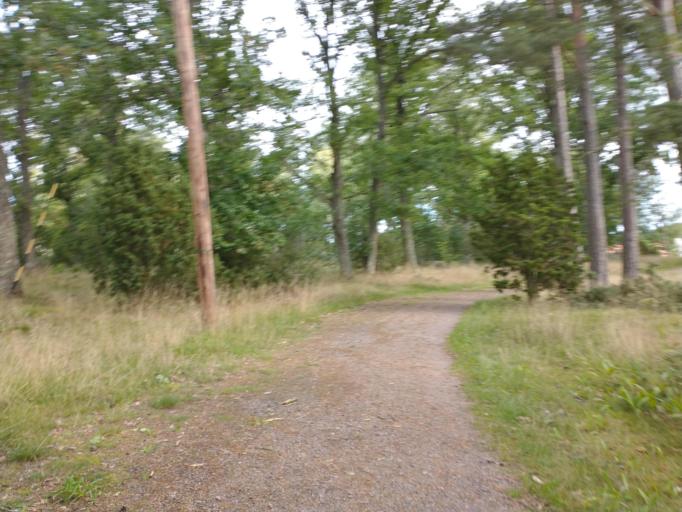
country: SE
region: Kalmar
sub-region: Kalmar Kommun
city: Lindsdal
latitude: 56.7772
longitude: 16.2997
